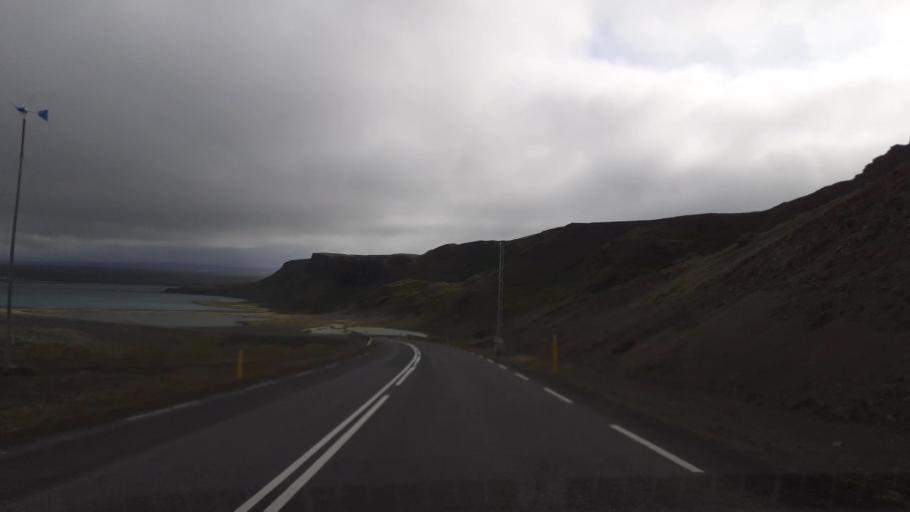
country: IS
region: Northeast
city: Husavik
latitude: 66.1304
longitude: -16.9526
